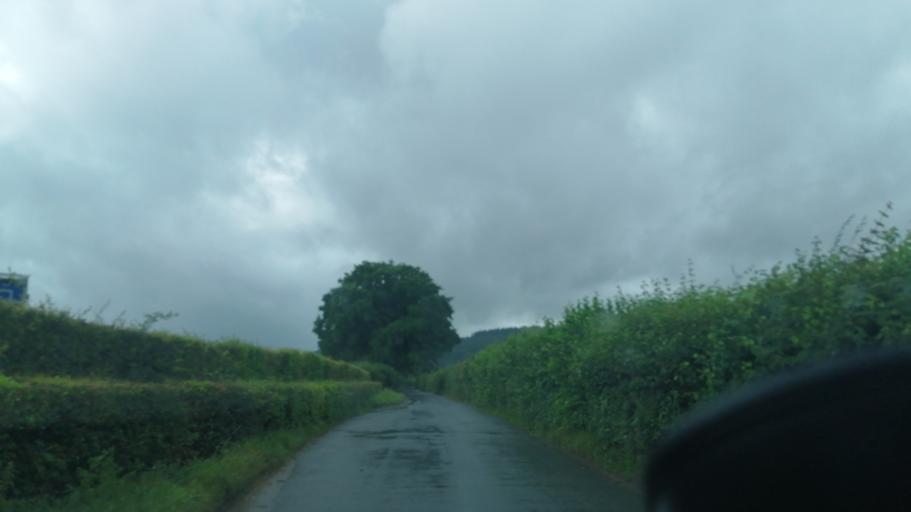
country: GB
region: England
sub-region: Herefordshire
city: Madley
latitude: 52.0287
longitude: -2.8550
